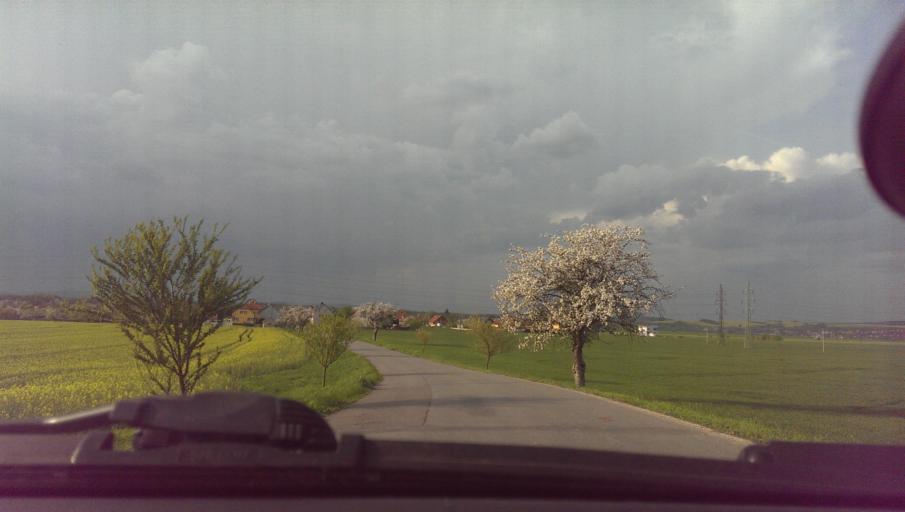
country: CZ
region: Zlin
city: Knezpole
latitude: 49.0923
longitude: 17.5202
